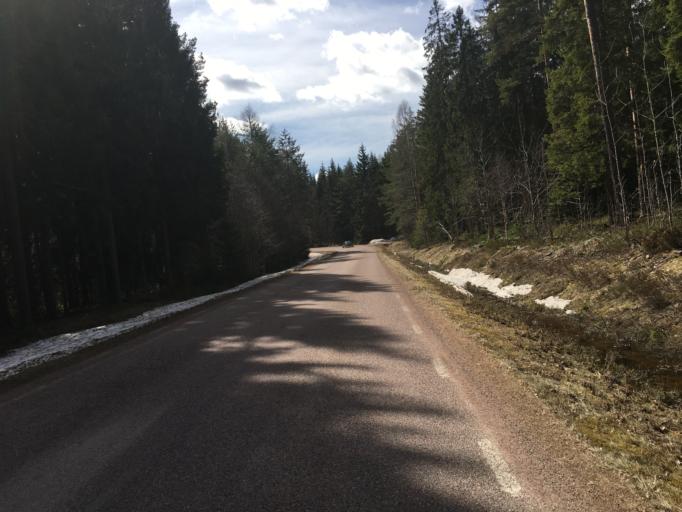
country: SE
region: Gaevleborg
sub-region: Hofors Kommun
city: Hofors
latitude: 60.4879
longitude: 16.4183
